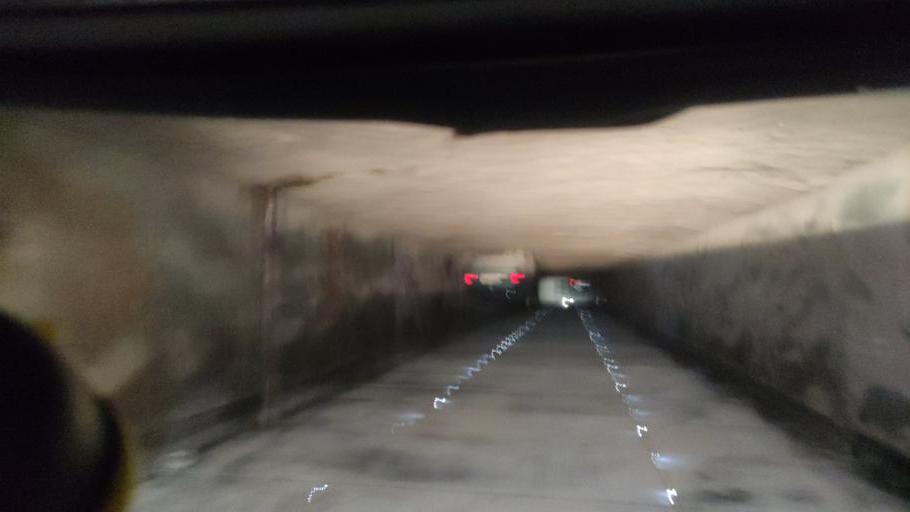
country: RU
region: Samara
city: Tol'yatti
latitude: 53.5492
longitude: 49.4639
